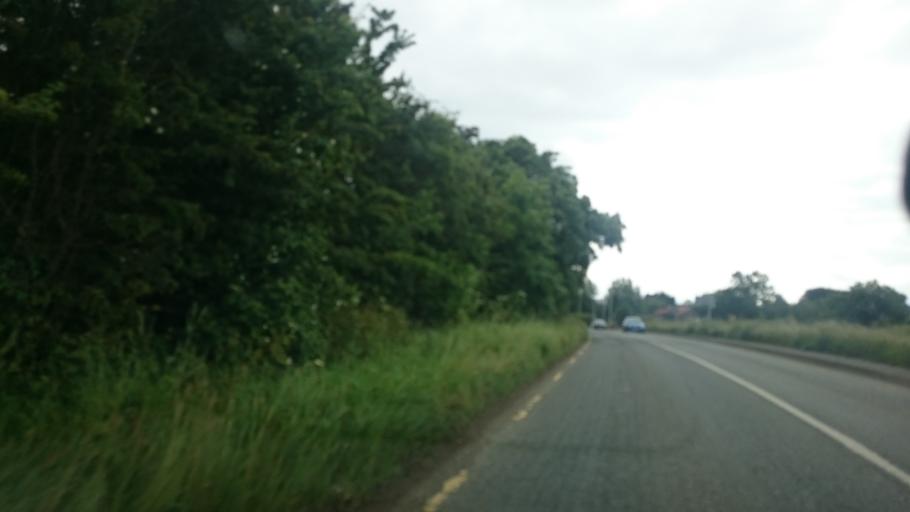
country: IE
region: Leinster
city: Lusk
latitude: 53.5326
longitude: -6.1645
